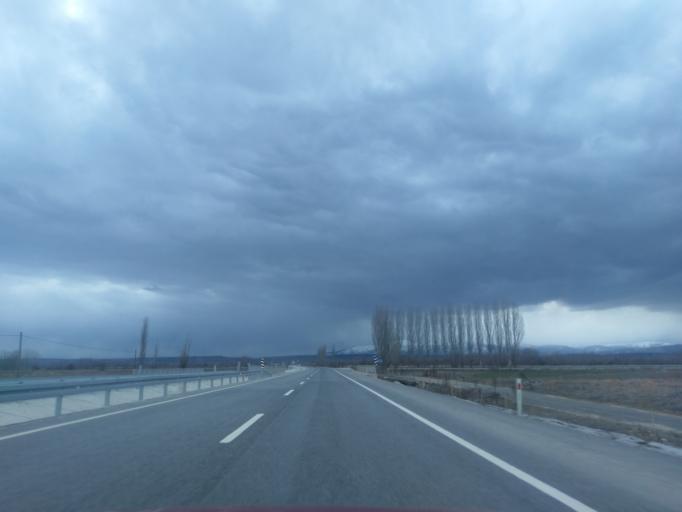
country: TR
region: Kuetahya
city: Cavdarhisar
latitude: 39.2113
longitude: 29.6502
